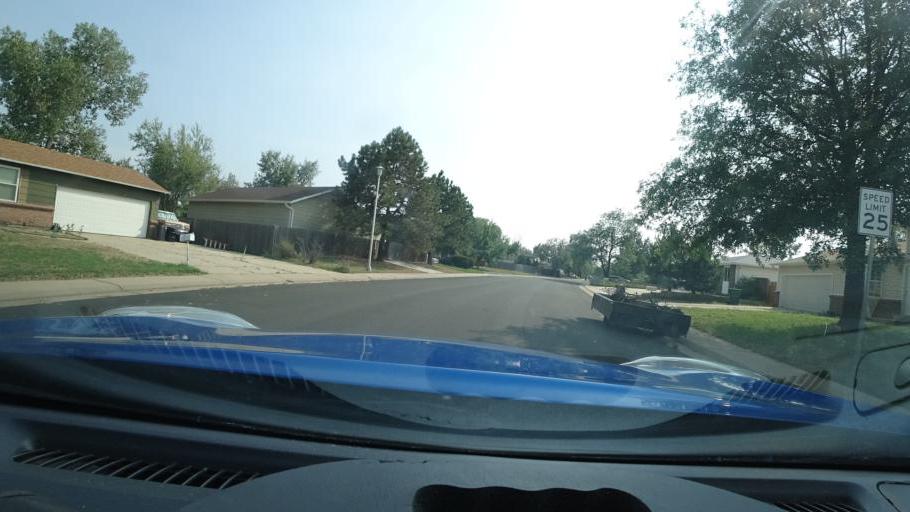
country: US
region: Colorado
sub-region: Adams County
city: Aurora
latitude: 39.6667
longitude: -104.8063
